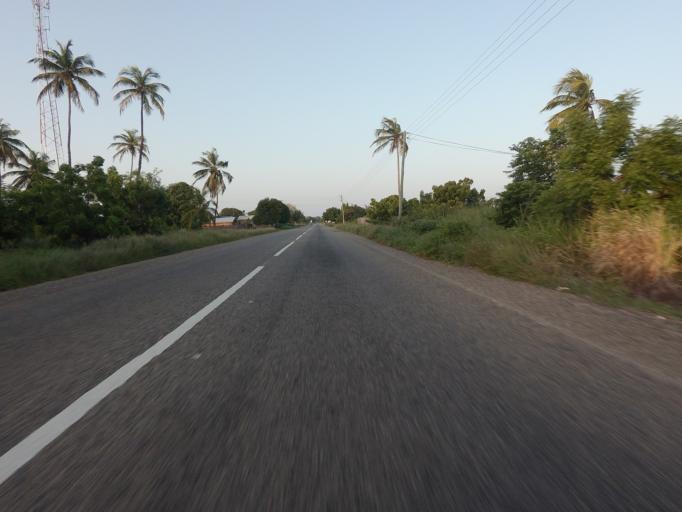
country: GH
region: Volta
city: Anloga
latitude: 5.7858
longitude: 0.8539
